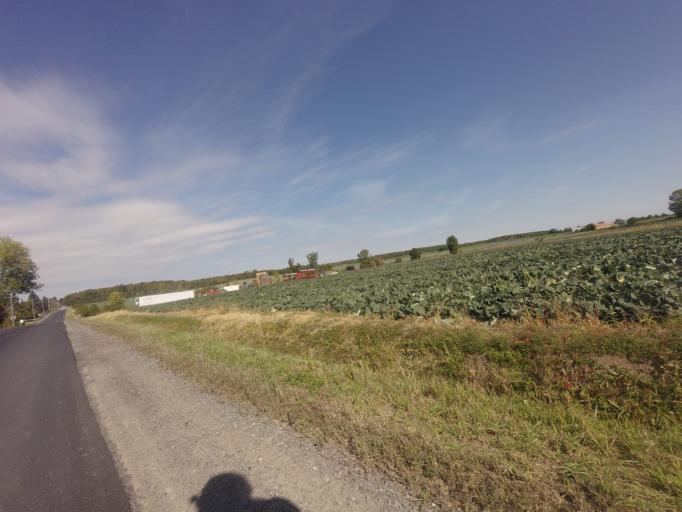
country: CA
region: Quebec
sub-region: Laurentides
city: Saint-Eustache
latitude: 45.5964
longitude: -73.9162
